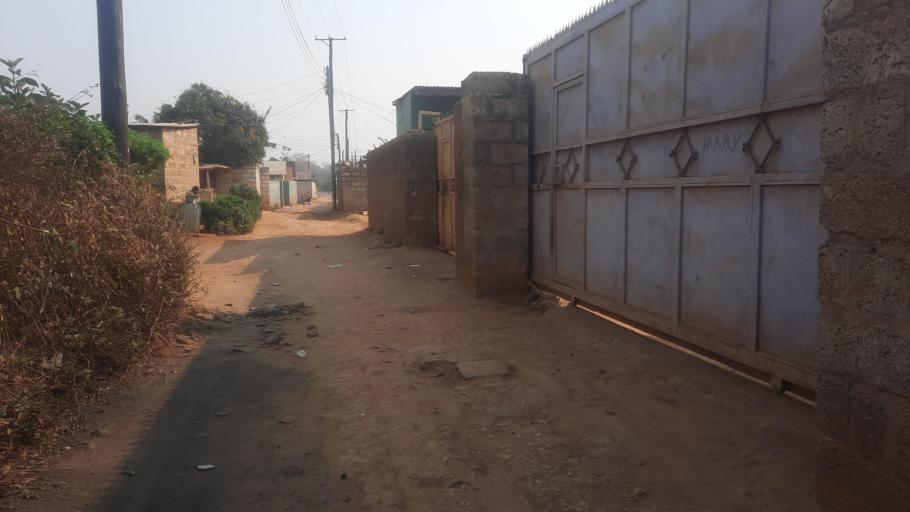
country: ZM
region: Lusaka
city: Lusaka
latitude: -15.3935
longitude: 28.3839
